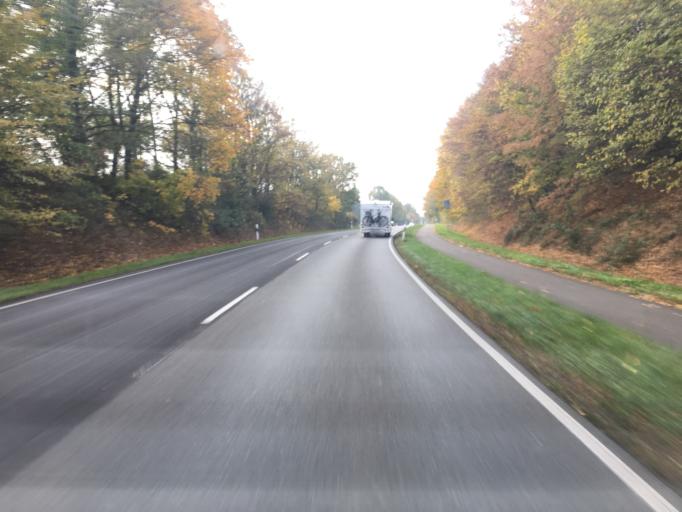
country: DE
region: North Rhine-Westphalia
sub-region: Regierungsbezirk Dusseldorf
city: Sonsbeck
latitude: 51.6293
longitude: 6.3988
